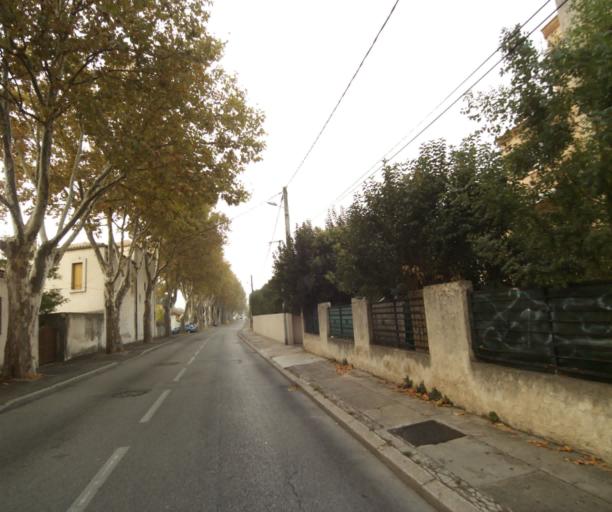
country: FR
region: Provence-Alpes-Cote d'Azur
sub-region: Departement des Bouches-du-Rhone
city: Marignane
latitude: 43.4130
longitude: 5.2127
